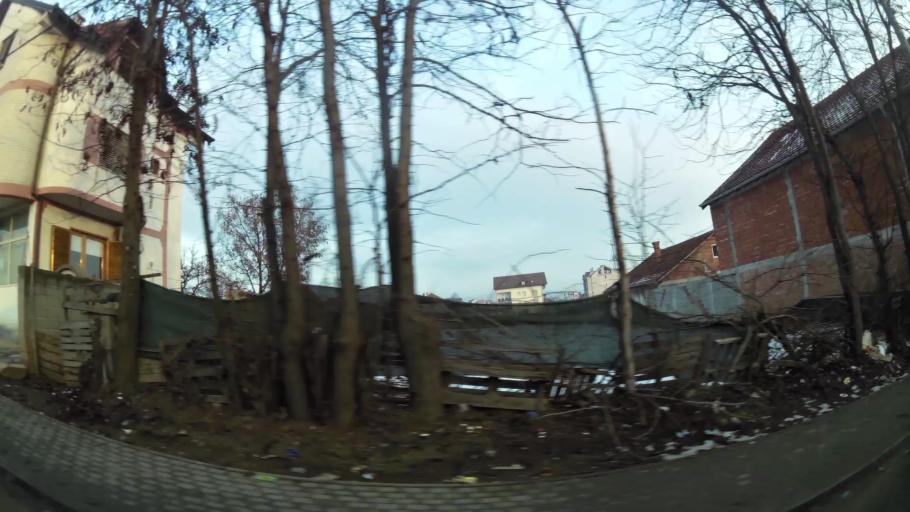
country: MK
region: Aracinovo
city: Arachinovo
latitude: 42.0277
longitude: 21.5643
